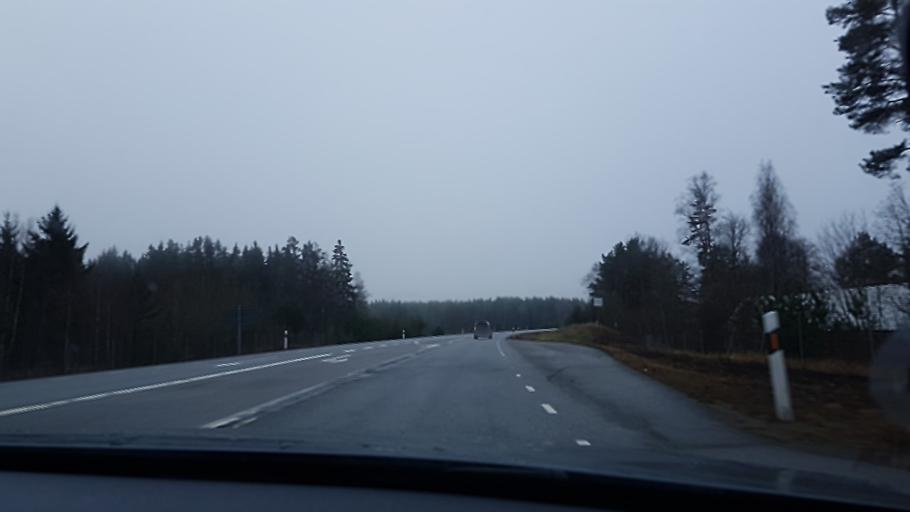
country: SE
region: Vaestra Goetaland
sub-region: Gullspangs Kommun
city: Gullspang
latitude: 58.8608
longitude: 14.0060
